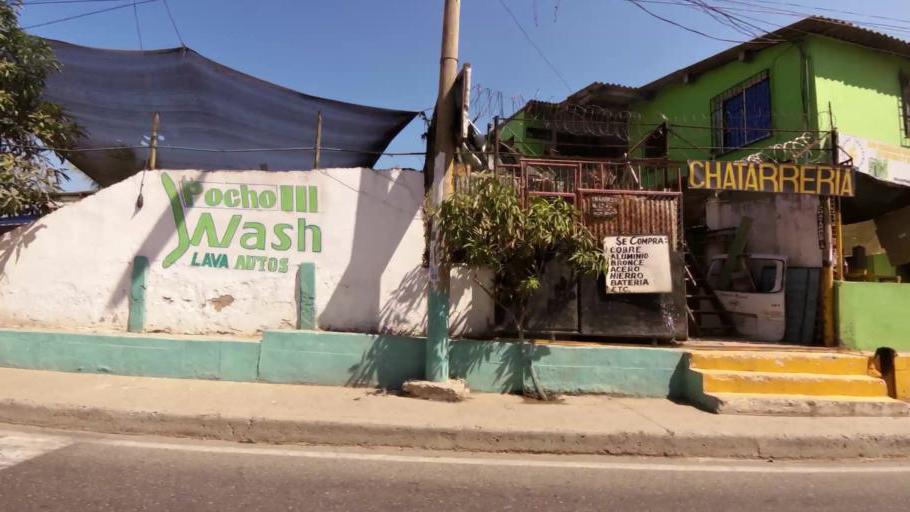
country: CO
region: Bolivar
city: Cartagena
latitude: 10.3888
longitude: -75.5141
